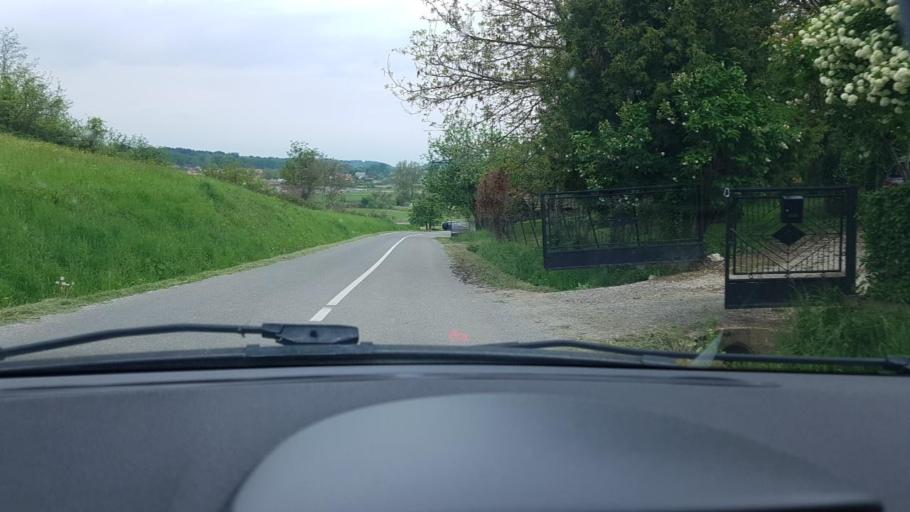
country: HR
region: Krapinsko-Zagorska
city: Selnica
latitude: 45.9857
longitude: 16.0145
